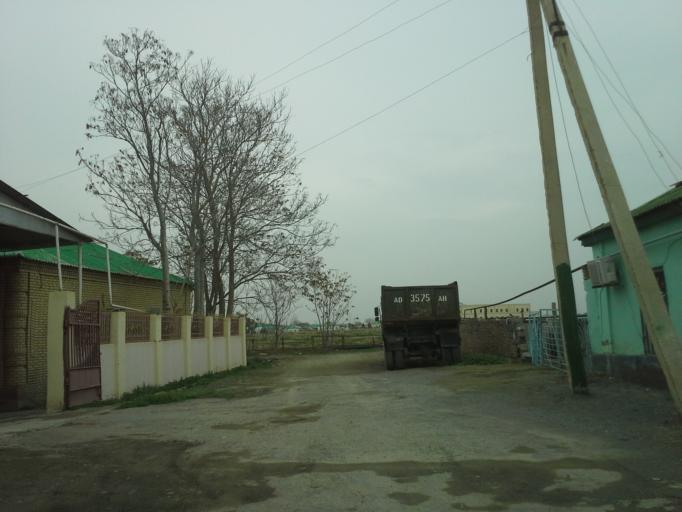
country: TM
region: Ahal
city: Abadan
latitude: 37.9679
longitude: 58.2222
